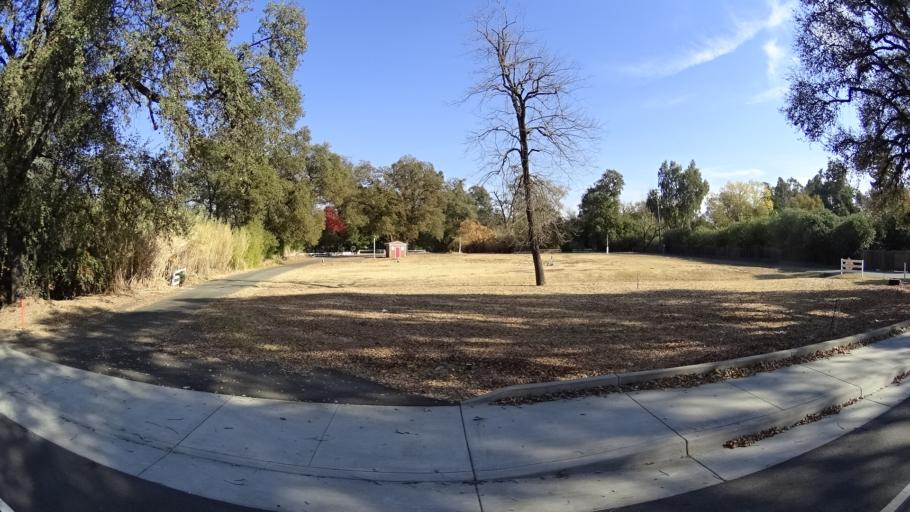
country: US
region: California
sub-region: Sacramento County
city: Citrus Heights
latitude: 38.6838
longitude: -121.2903
